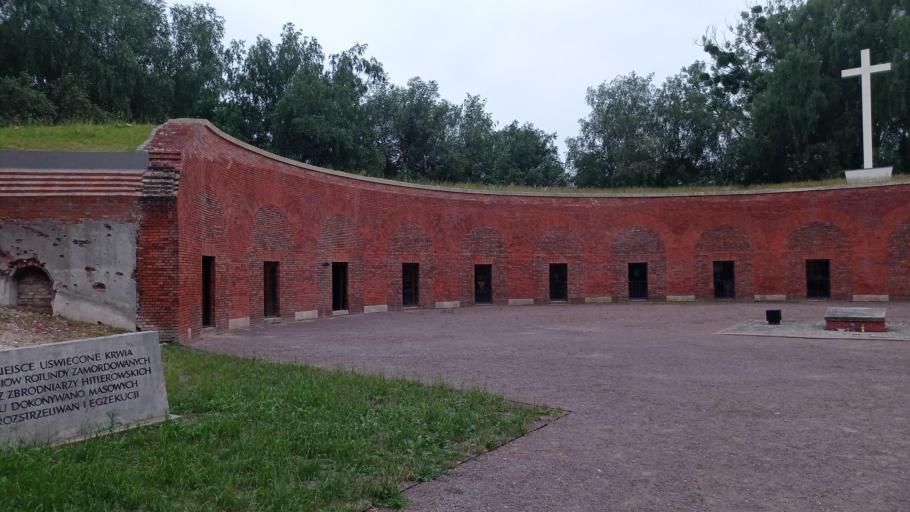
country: PL
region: Lublin Voivodeship
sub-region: Zamosc
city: Zamosc
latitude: 50.7109
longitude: 23.2473
